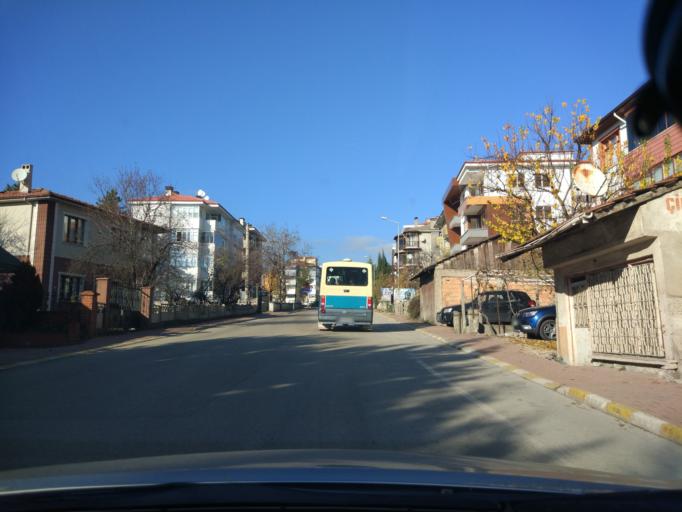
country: TR
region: Karabuk
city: Safranbolu
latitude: 41.2481
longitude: 32.6746
